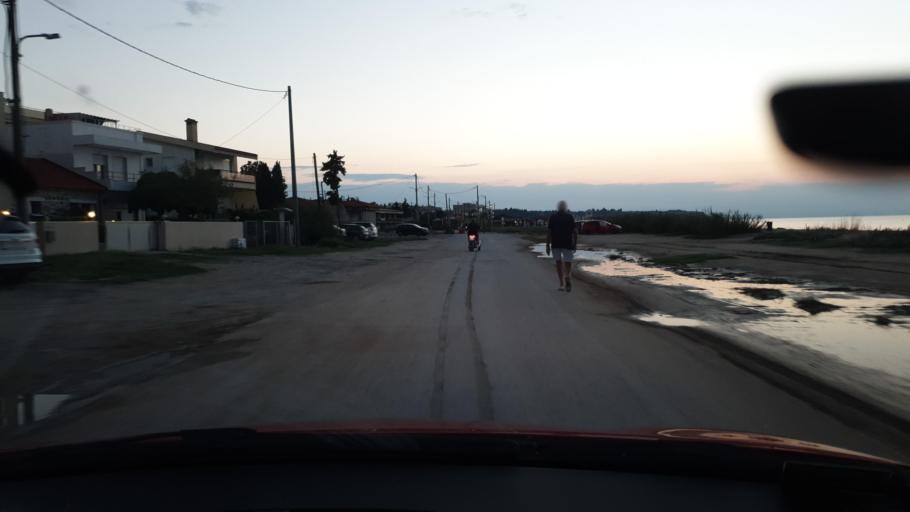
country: GR
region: Central Macedonia
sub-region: Nomos Thessalonikis
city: Neoi Epivates
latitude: 40.5024
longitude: 22.8943
